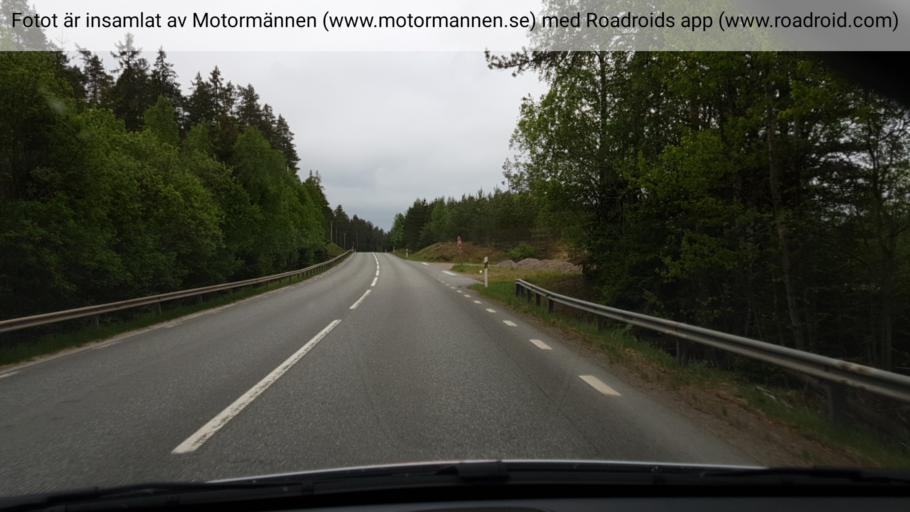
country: SE
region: Joenkoeping
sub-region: Mullsjo Kommun
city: Mullsjoe
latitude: 57.7889
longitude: 13.8358
